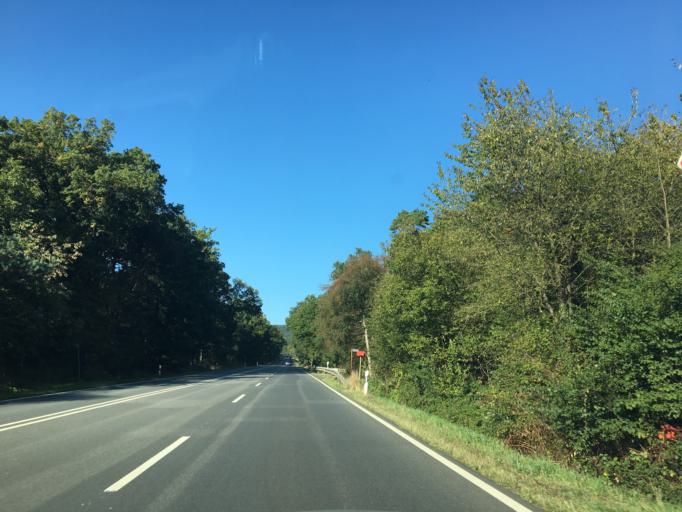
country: DE
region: Hesse
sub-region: Regierungsbezirk Darmstadt
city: Bad Homburg vor der Hoehe
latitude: 50.2497
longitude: 8.5908
